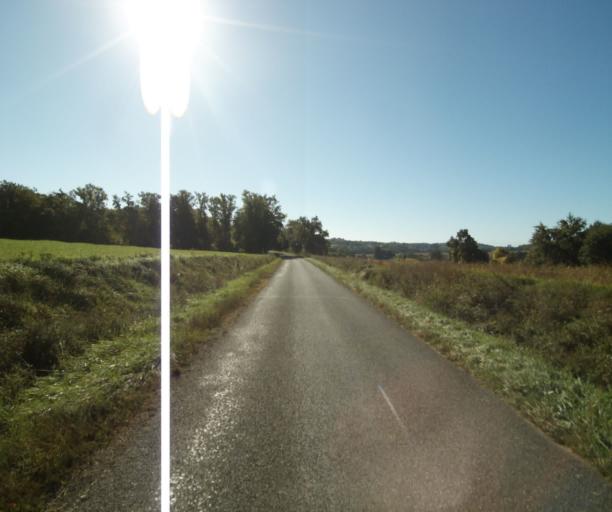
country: FR
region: Midi-Pyrenees
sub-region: Departement du Gers
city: Gondrin
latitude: 43.8178
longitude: 0.2198
